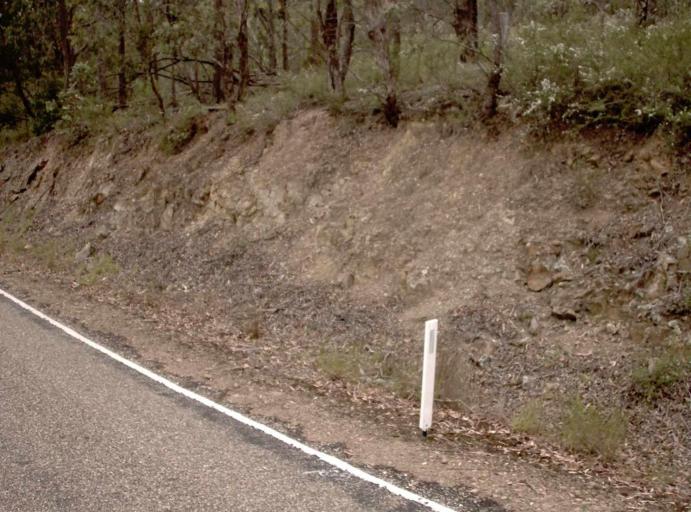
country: AU
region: Victoria
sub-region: East Gippsland
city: Bairnsdale
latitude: -37.5379
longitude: 147.2089
